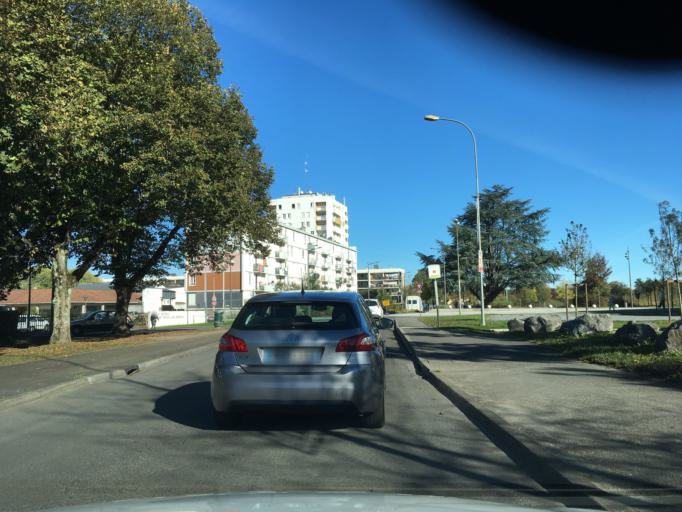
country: FR
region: Aquitaine
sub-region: Departement des Pyrenees-Atlantiques
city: Pau
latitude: 43.3199
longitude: -0.3438
